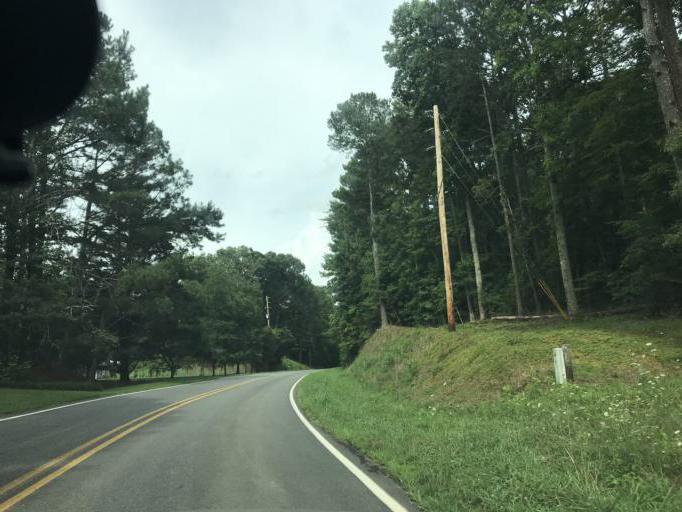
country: US
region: Georgia
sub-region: Dawson County
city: Dawsonville
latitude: 34.3280
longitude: -84.1809
